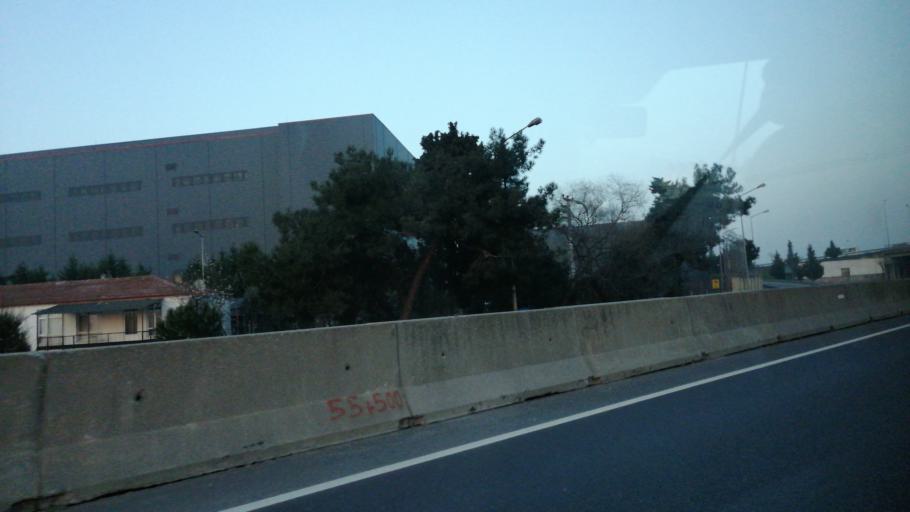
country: TR
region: Yalova
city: Taskopru
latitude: 40.6875
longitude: 29.4304
